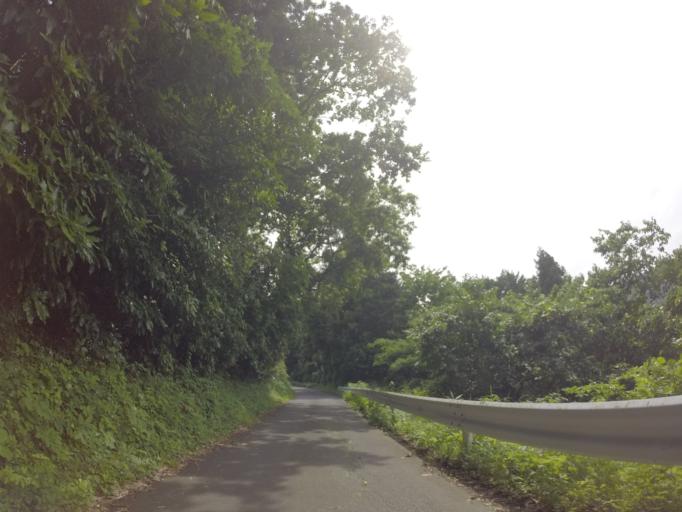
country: JP
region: Shizuoka
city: Fujinomiya
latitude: 35.2791
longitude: 138.5698
